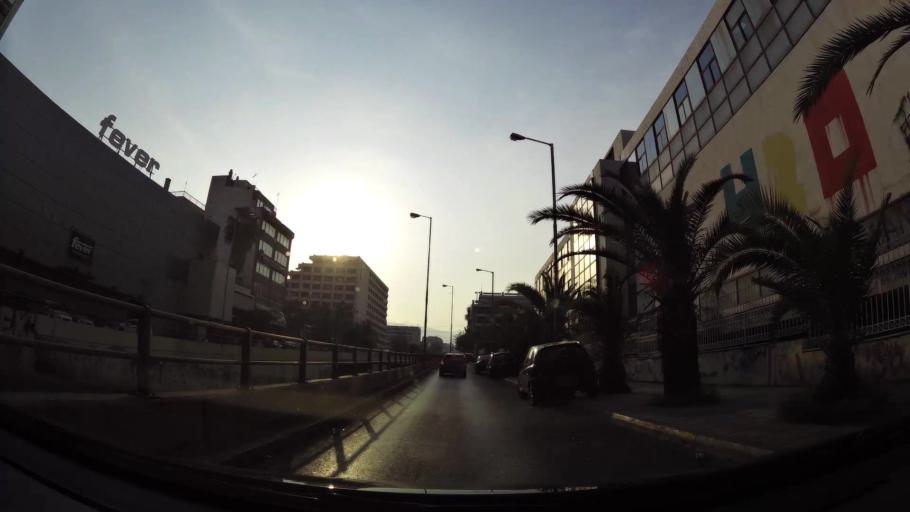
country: GR
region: Attica
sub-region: Nomarchia Athinas
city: Nea Smyrni
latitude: 37.9602
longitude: 23.7194
